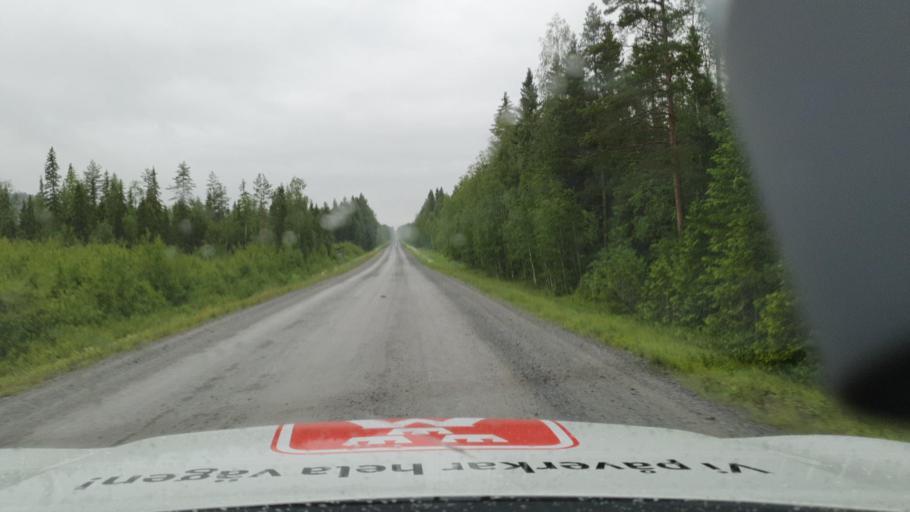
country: SE
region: Vaesterbotten
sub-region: Nordmalings Kommun
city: Nordmaling
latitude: 63.8373
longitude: 19.4844
